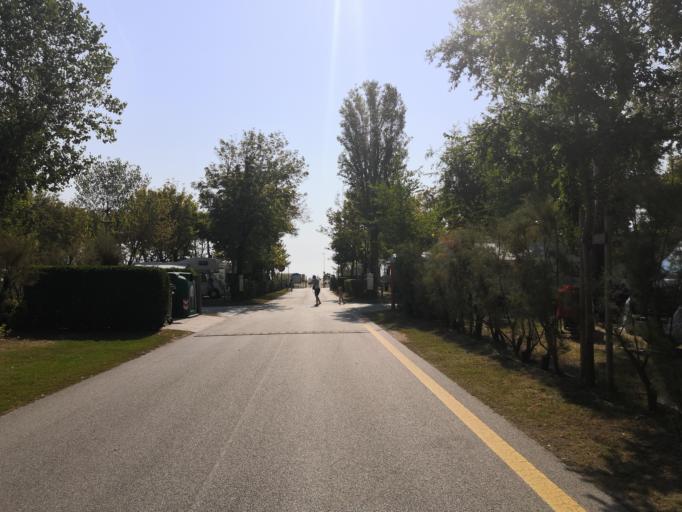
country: IT
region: Veneto
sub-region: Provincia di Venezia
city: Ca' Savio
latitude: 45.4342
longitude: 12.4402
